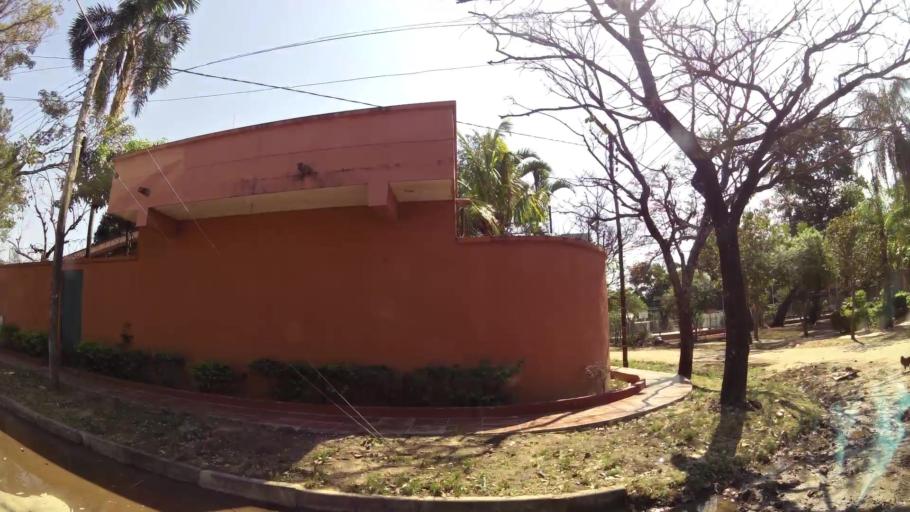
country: BO
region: Santa Cruz
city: Santa Cruz de la Sierra
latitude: -17.7339
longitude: -63.1589
